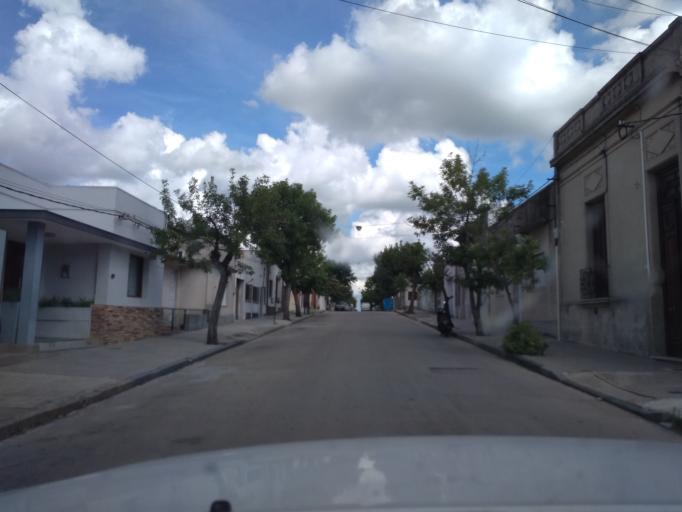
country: UY
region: Florida
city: Florida
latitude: -34.0986
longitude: -56.2122
